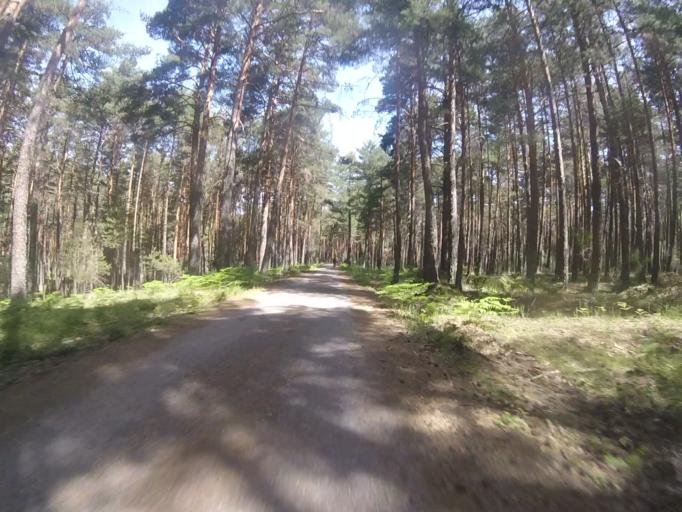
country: ES
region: Madrid
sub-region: Provincia de Madrid
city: Cercedilla
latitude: 40.8146
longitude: -4.0288
